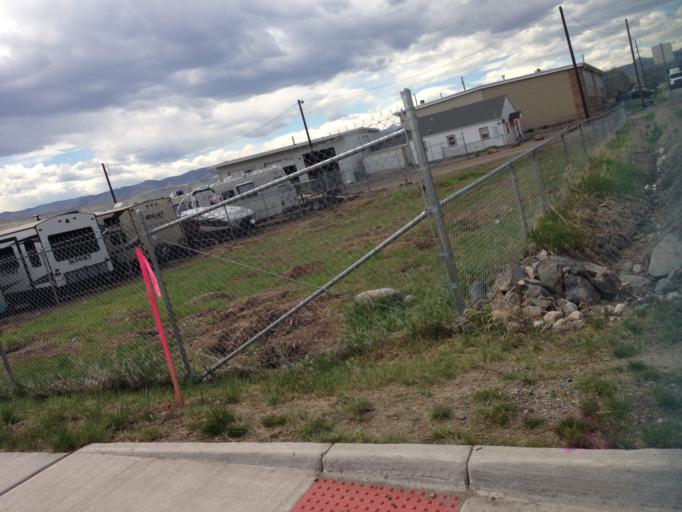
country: US
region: Colorado
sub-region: Jefferson County
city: Applewood
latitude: 39.7909
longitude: -105.1325
